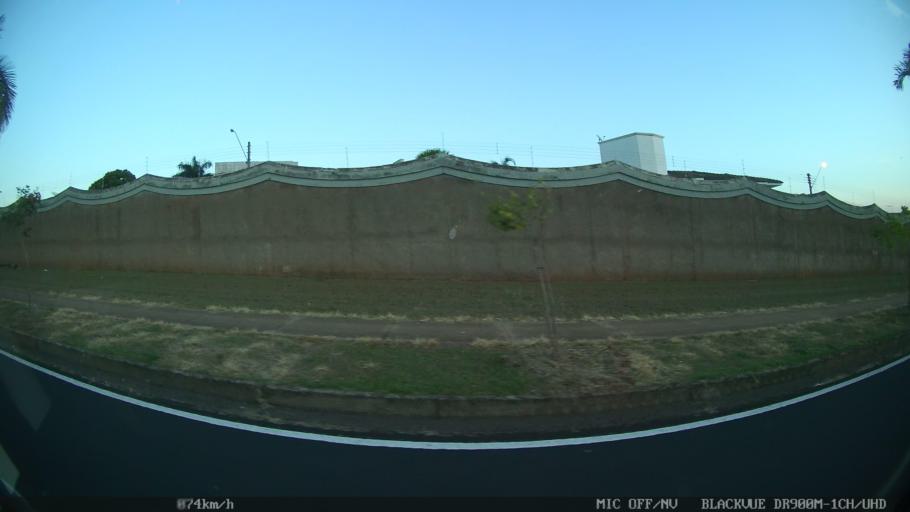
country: BR
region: Sao Paulo
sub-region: Sao Jose Do Rio Preto
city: Sao Jose do Rio Preto
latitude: -20.8171
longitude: -49.3414
